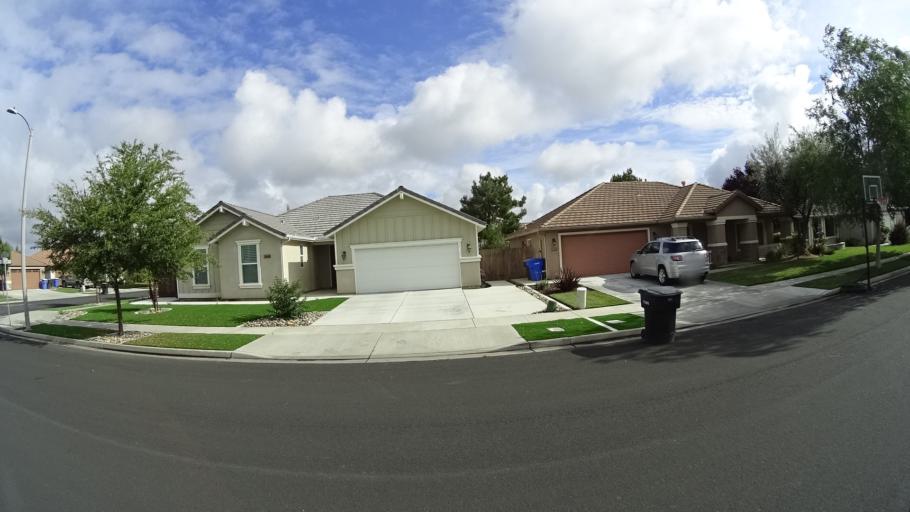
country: US
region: California
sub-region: Kings County
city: Lucerne
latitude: 36.3535
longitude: -119.6676
